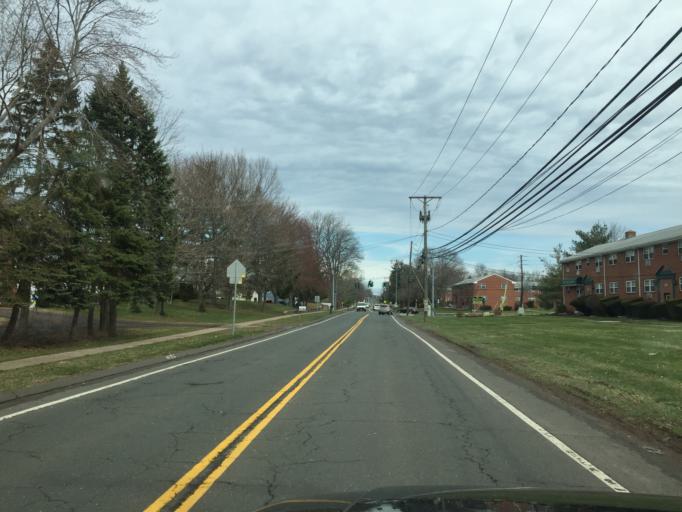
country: US
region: Connecticut
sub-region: Hartford County
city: Newington
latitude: 41.6674
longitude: -72.7276
